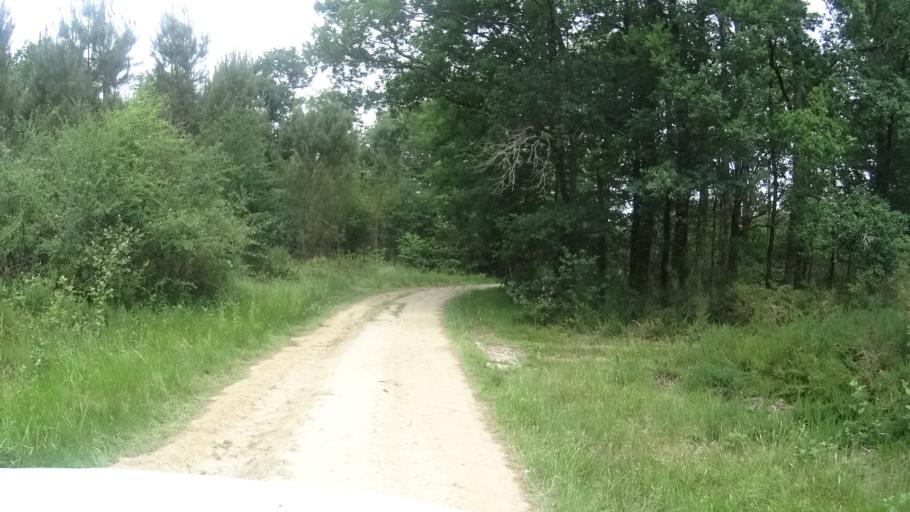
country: FR
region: Aquitaine
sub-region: Departement de la Dordogne
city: Riberac
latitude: 45.1555
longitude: 0.2694
